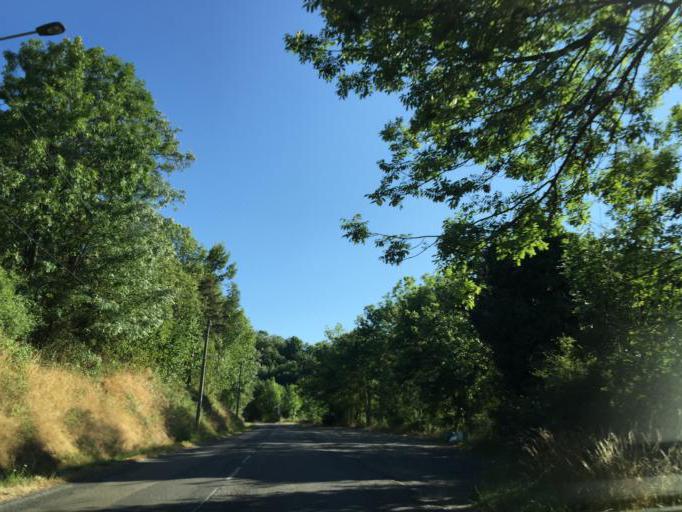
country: FR
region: Rhone-Alpes
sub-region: Departement de la Loire
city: Saint-Jean-Bonnefonds
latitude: 45.4360
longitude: 4.4564
